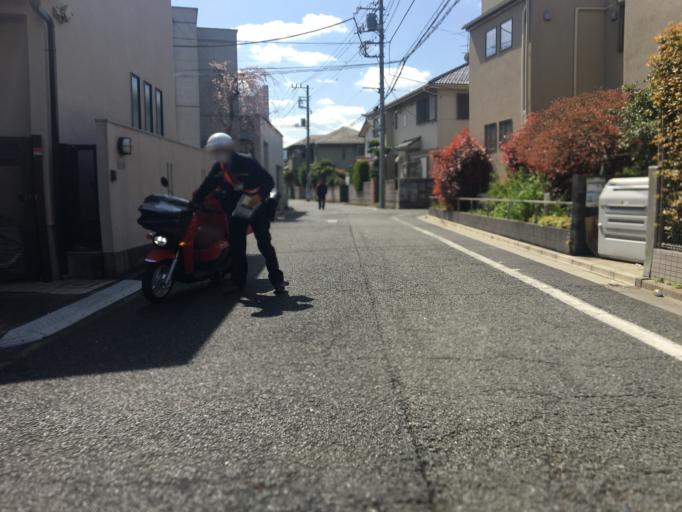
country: JP
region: Tokyo
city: Musashino
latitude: 35.7285
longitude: 139.5953
